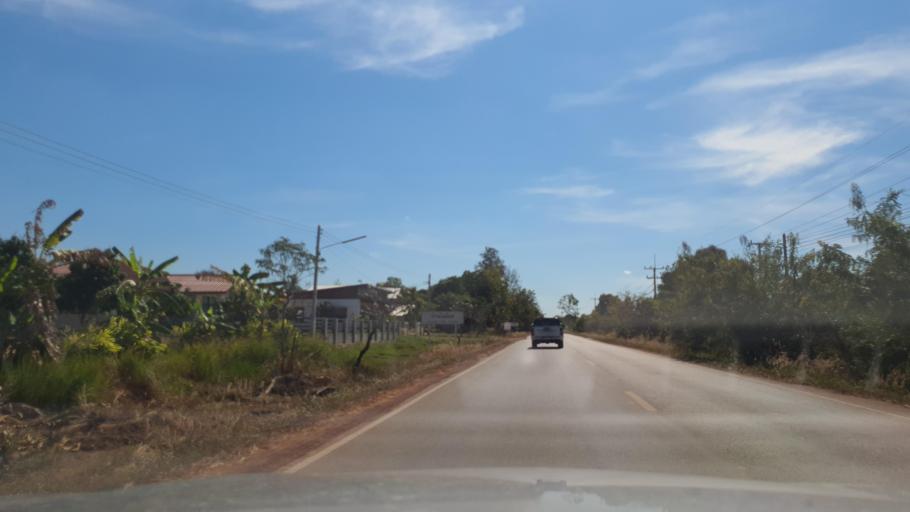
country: TH
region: Sakon Nakhon
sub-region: Amphoe Khok Si Suphan
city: Khok Si Suphan
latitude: 17.0635
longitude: 104.2143
